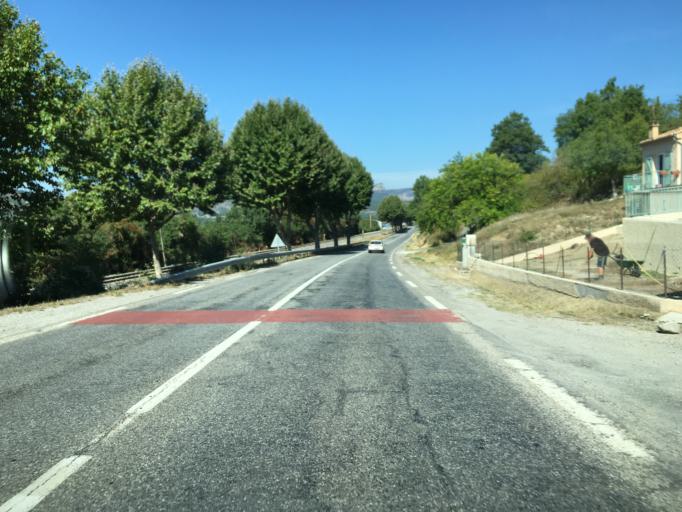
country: FR
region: Provence-Alpes-Cote d'Azur
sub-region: Departement des Hautes-Alpes
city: Laragne-Monteglin
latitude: 44.3181
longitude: 5.8120
